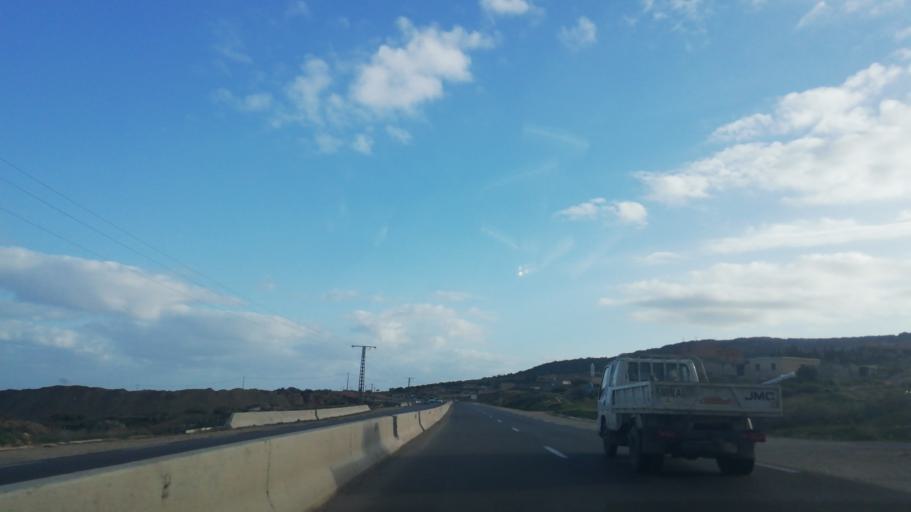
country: DZ
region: Mostaganem
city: Mostaganem
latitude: 36.0976
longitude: 0.2099
